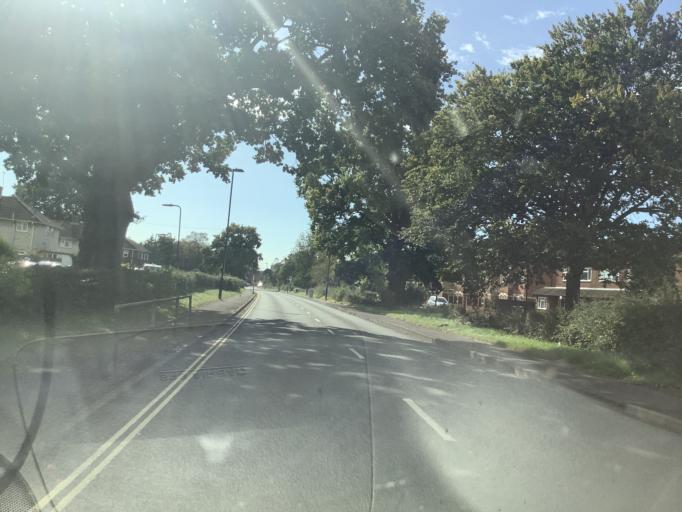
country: GB
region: England
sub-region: Hampshire
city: Marchwood
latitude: 50.9234
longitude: -1.4551
